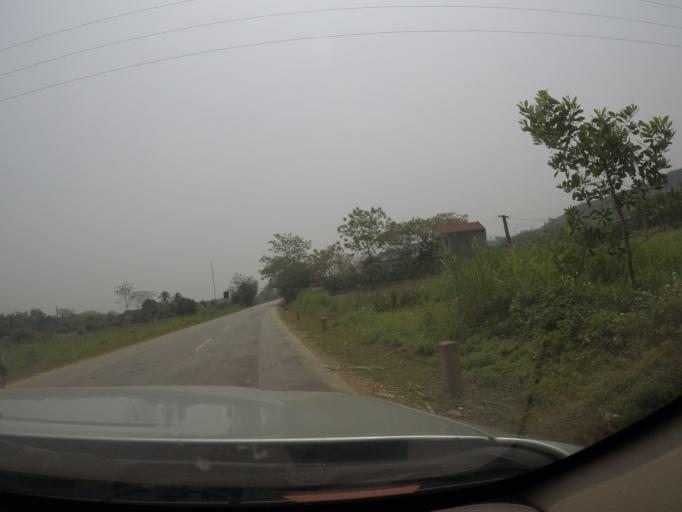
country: VN
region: Thanh Hoa
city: Thi Tran Thuong Xuan
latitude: 19.9923
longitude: 105.4032
